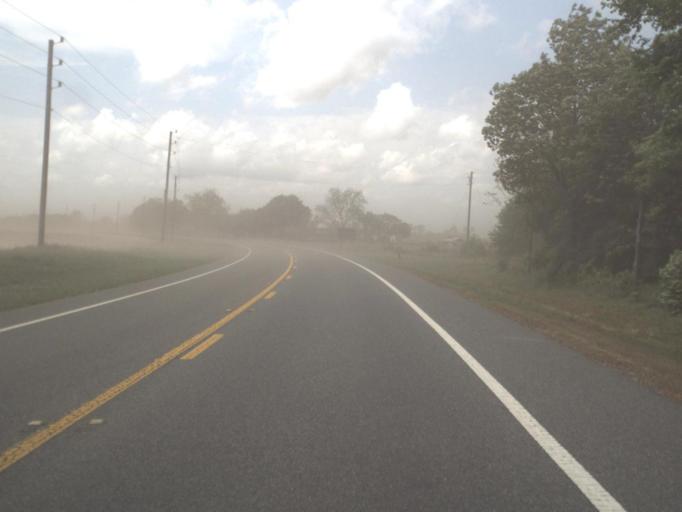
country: US
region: Florida
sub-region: Santa Rosa County
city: Point Baker
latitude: 30.8058
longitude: -87.0974
